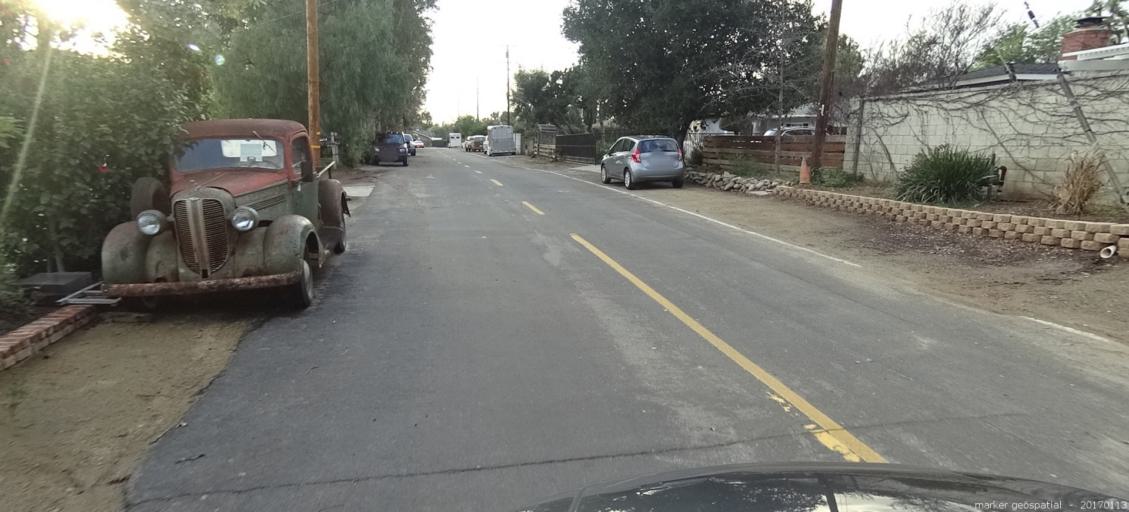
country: US
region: California
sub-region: Orange County
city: Villa Park
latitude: 33.8119
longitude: -117.7806
